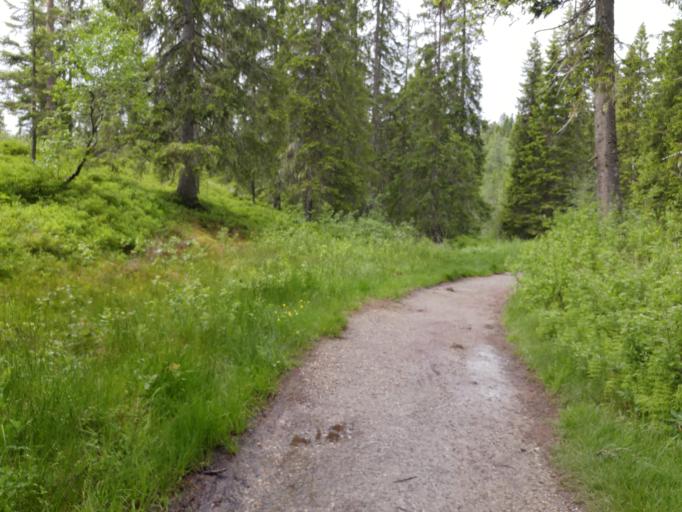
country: NO
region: Sor-Trondelag
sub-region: Melhus
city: Melhus
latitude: 63.4017
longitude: 10.2586
